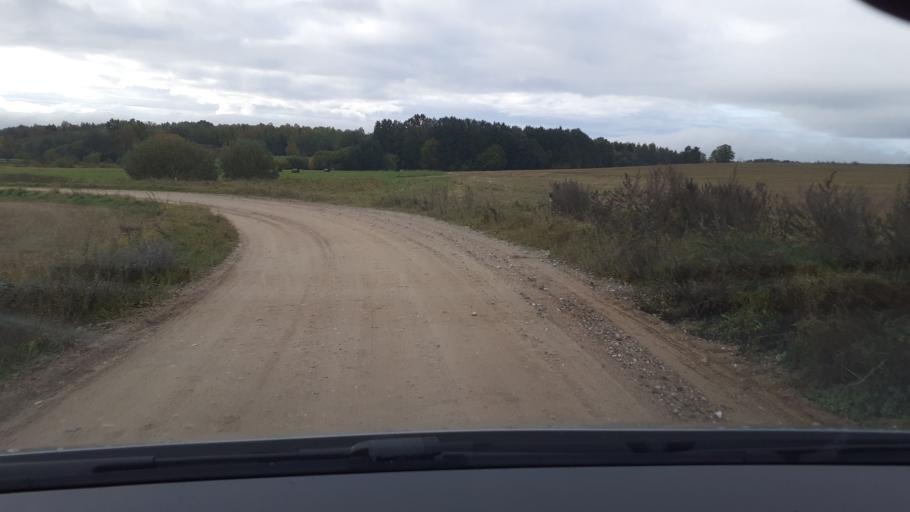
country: LV
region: Kuldigas Rajons
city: Kuldiga
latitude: 57.0141
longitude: 21.9152
